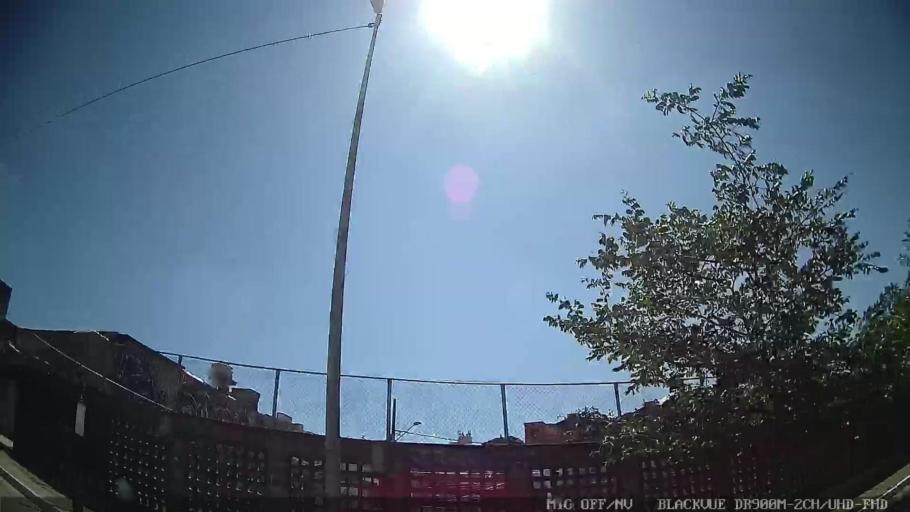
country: BR
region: Sao Paulo
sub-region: Sao Caetano Do Sul
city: Sao Caetano do Sul
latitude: -23.5740
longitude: -46.5201
